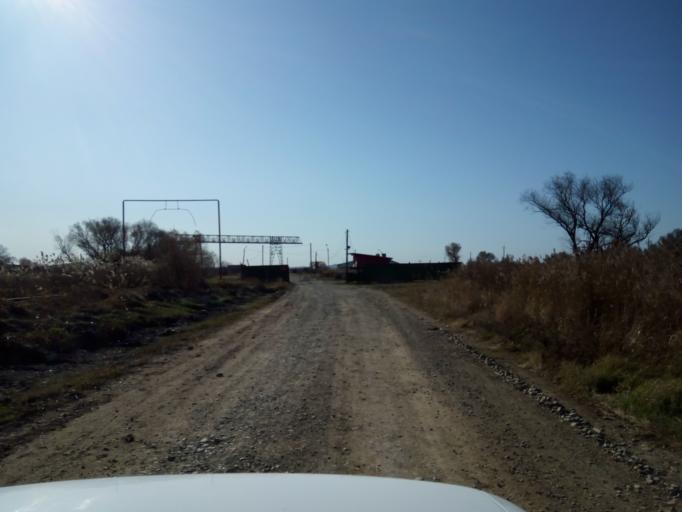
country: RU
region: Primorskiy
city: Dal'nerechensk
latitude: 45.9062
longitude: 133.7960
